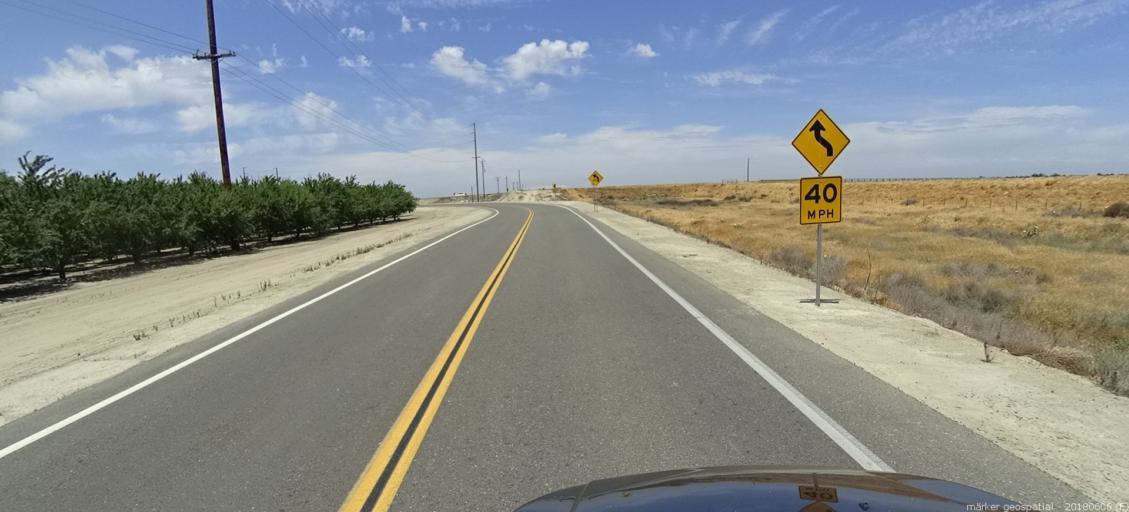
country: US
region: California
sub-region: Fresno County
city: Mendota
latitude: 36.8493
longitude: -120.3169
